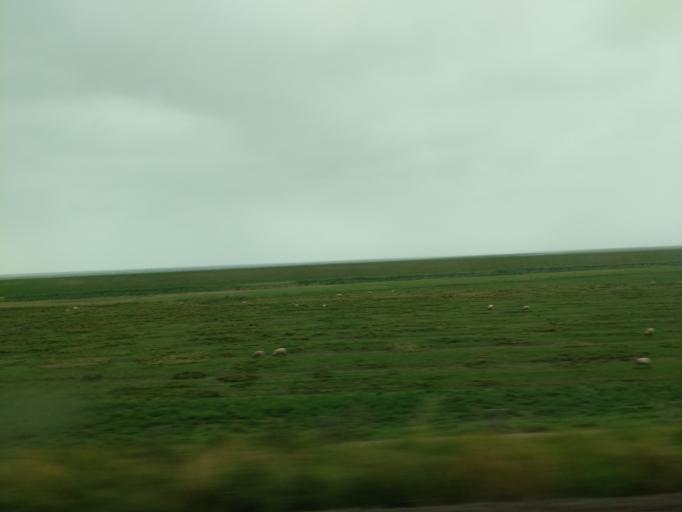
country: DE
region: Schleswig-Holstein
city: Friedrich-Wilhelm-Lubke-Koog
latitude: 54.8875
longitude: 8.6168
